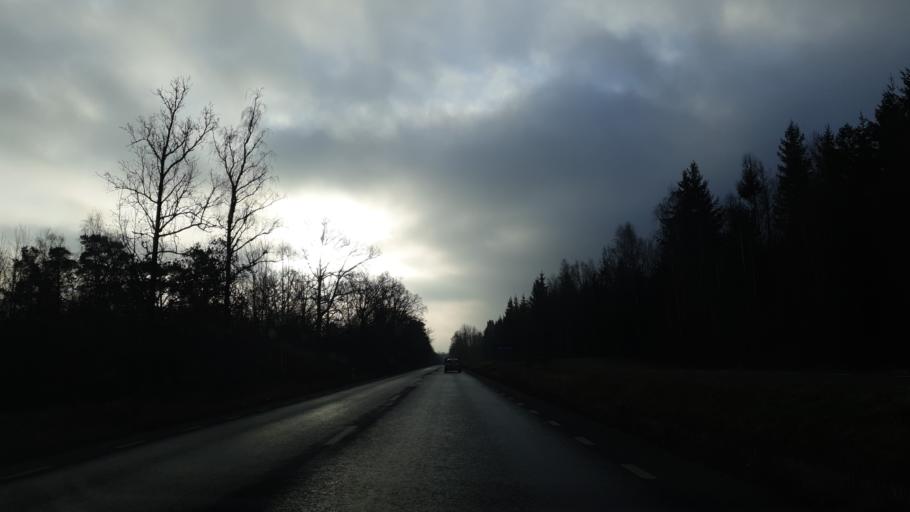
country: SE
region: Blekinge
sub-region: Karlshamns Kommun
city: Morrum
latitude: 56.1421
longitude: 14.6699
